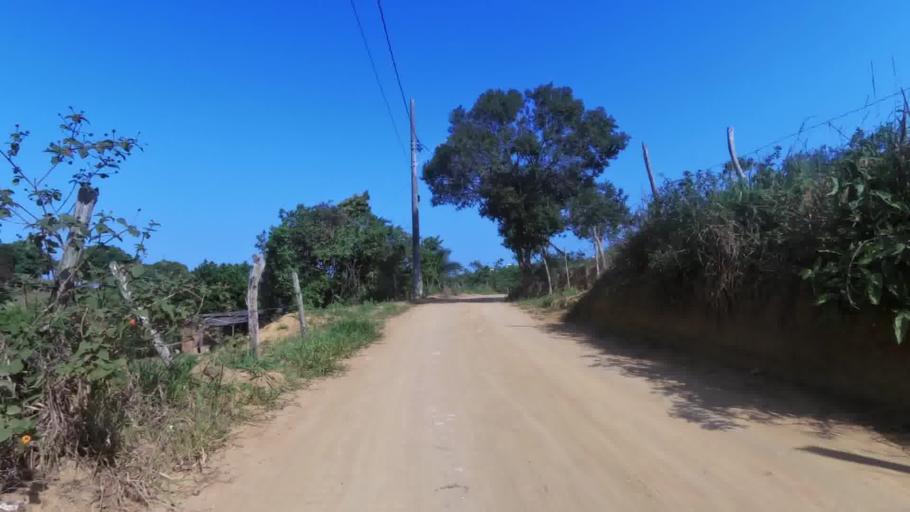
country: BR
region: Espirito Santo
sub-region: Piuma
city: Piuma
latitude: -20.8284
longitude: -40.7096
